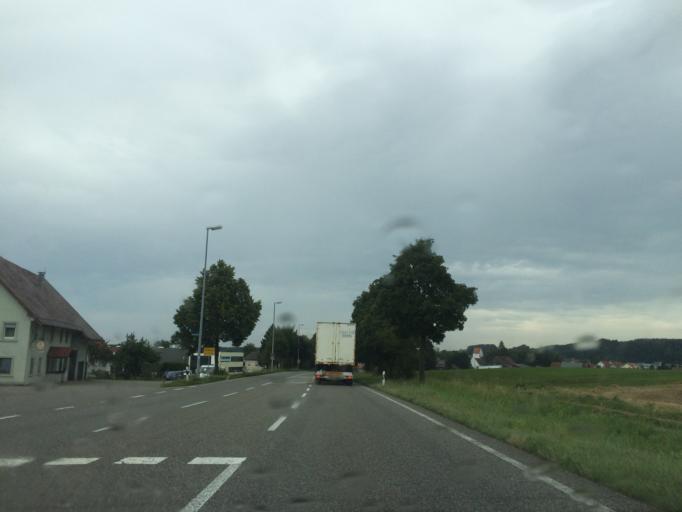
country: DE
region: Baden-Wuerttemberg
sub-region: Tuebingen Region
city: Bad Waldsee
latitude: 47.8914
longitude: 9.7167
